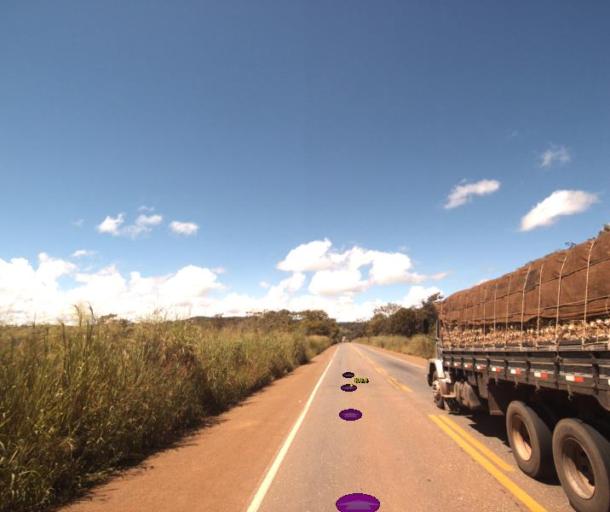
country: BR
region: Goias
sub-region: Pirenopolis
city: Pirenopolis
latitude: -16.0861
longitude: -49.0402
